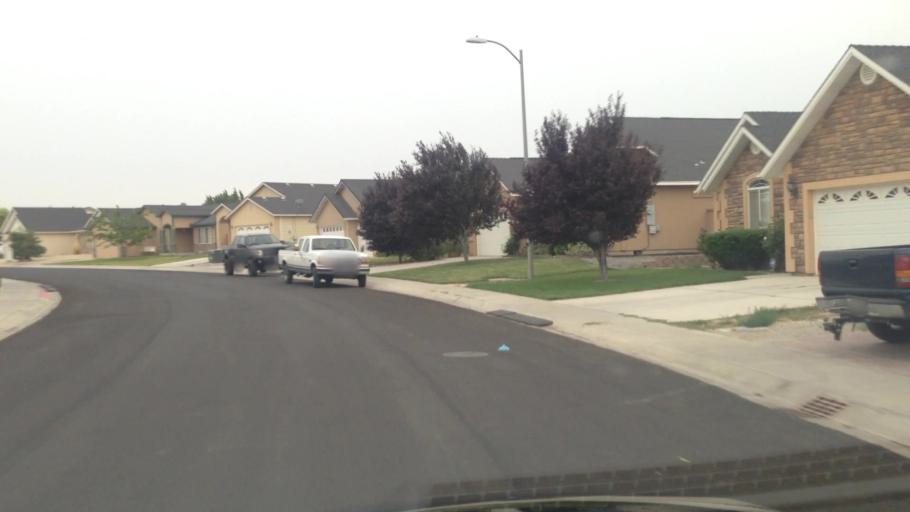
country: US
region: Nevada
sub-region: Lyon County
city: Fernley
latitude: 39.5892
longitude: -119.1539
